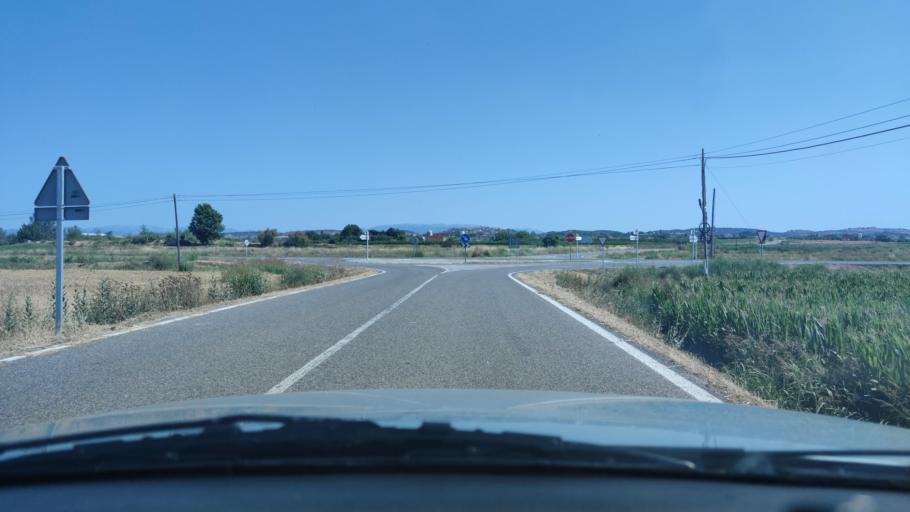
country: ES
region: Catalonia
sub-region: Provincia de Lleida
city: Penelles
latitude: 41.7414
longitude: 0.9482
